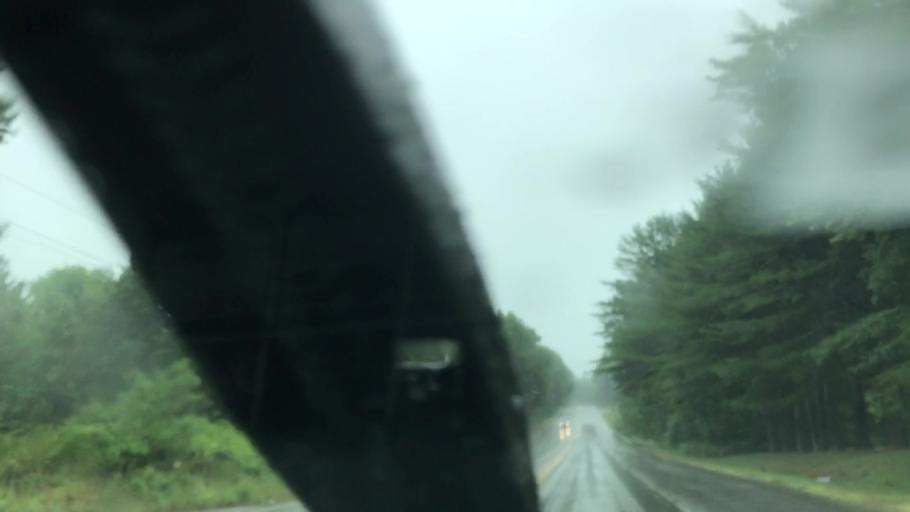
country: US
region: Maine
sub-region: York County
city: North Berwick
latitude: 43.3049
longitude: -70.7026
